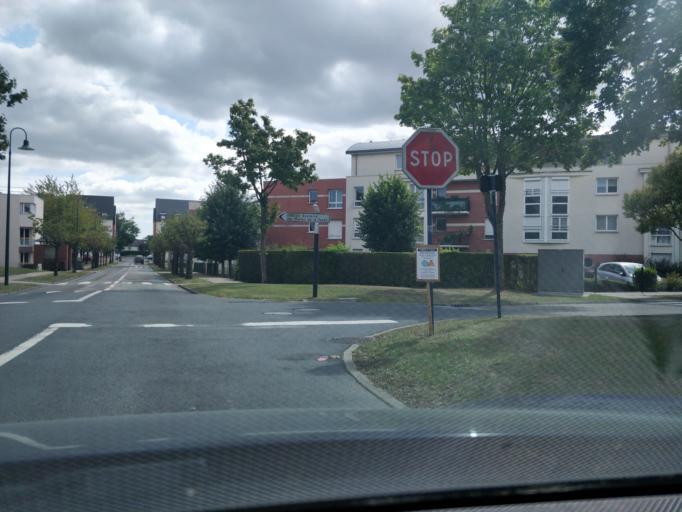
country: FR
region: Haute-Normandie
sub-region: Departement de la Seine-Maritime
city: Bois-Guillaume
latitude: 49.4803
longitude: 1.1108
